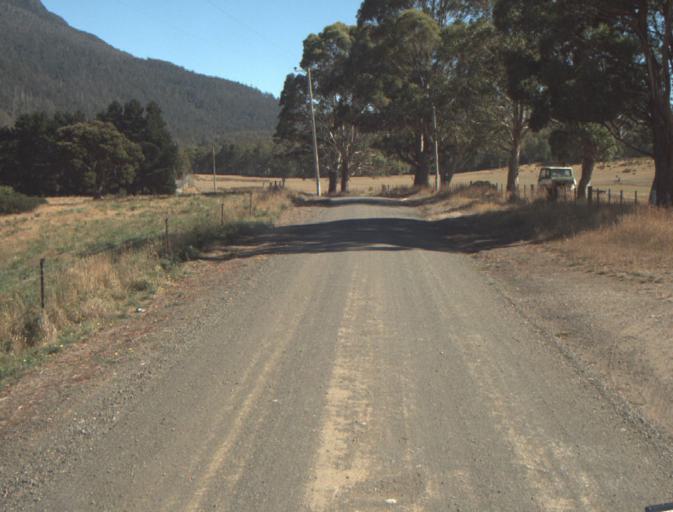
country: AU
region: Tasmania
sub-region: Launceston
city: Newstead
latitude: -41.3118
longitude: 147.3212
